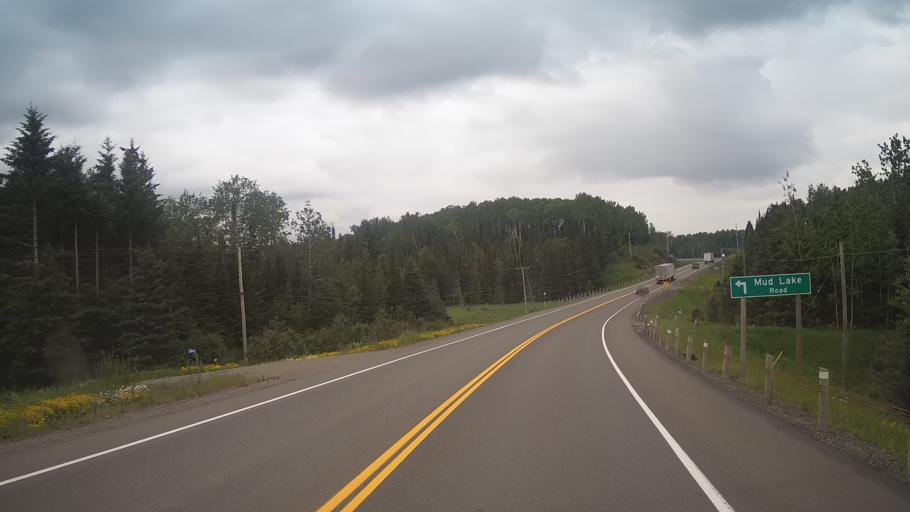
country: CA
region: Ontario
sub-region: Thunder Bay District
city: Thunder Bay
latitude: 48.5146
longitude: -89.5021
